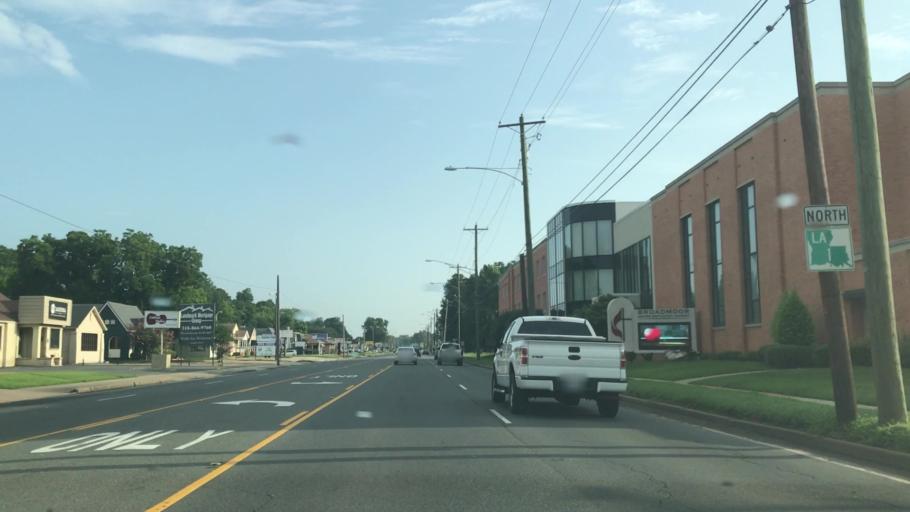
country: US
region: Louisiana
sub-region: Bossier Parish
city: Bossier City
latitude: 32.4712
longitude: -93.7221
